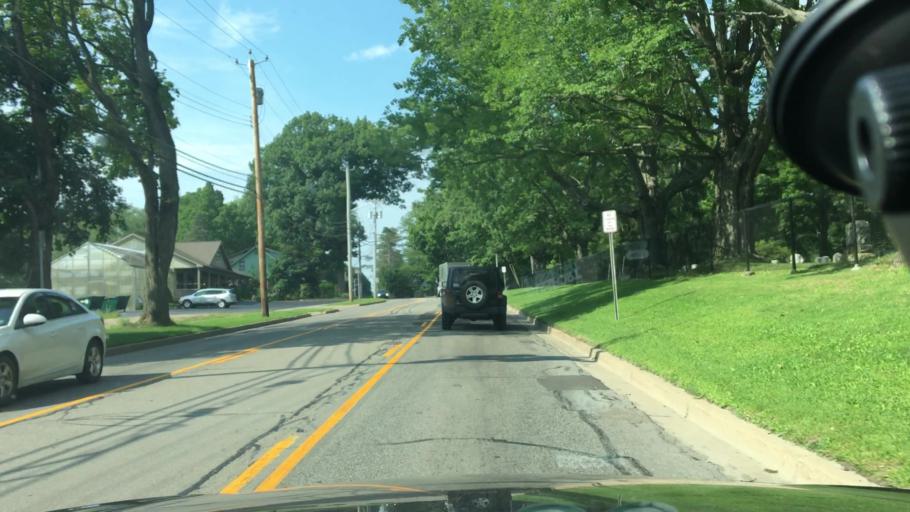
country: US
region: New York
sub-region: Chautauqua County
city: Jamestown
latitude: 42.1137
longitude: -79.2406
